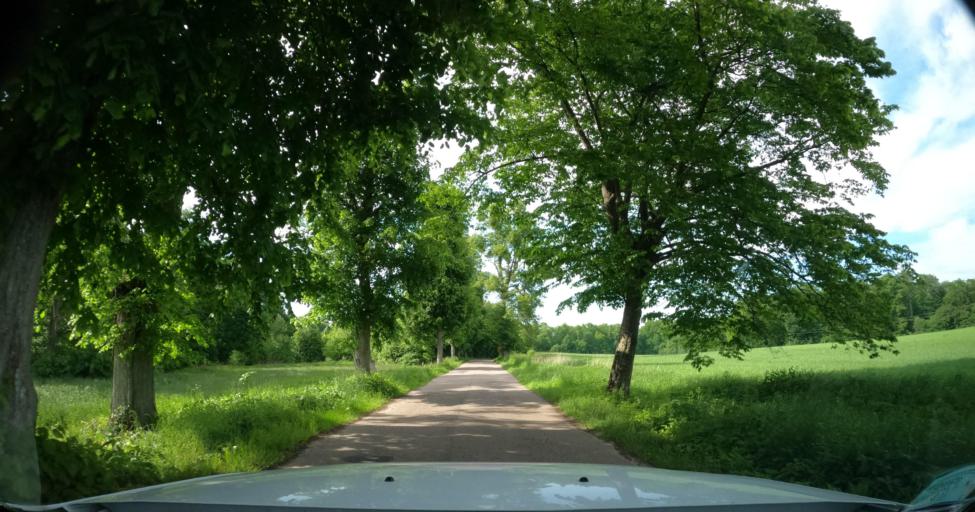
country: PL
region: Warmian-Masurian Voivodeship
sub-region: Powiat ostrodzki
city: Morag
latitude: 54.0240
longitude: 19.9125
